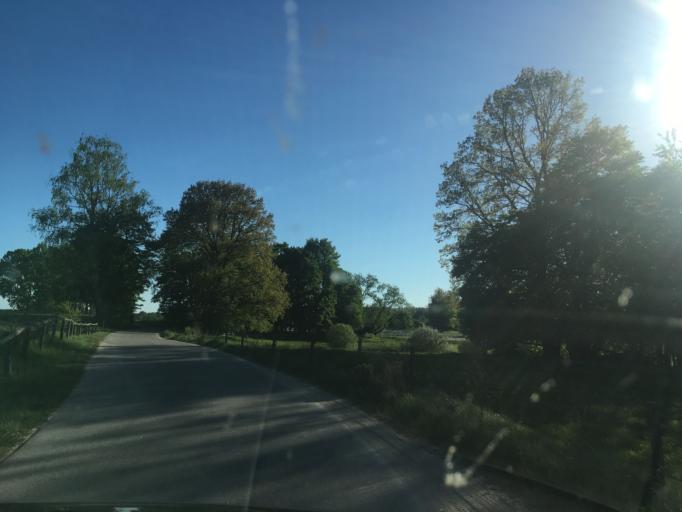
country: PL
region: Warmian-Masurian Voivodeship
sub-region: Powiat piski
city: Ruciane-Nida
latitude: 53.6883
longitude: 21.4741
